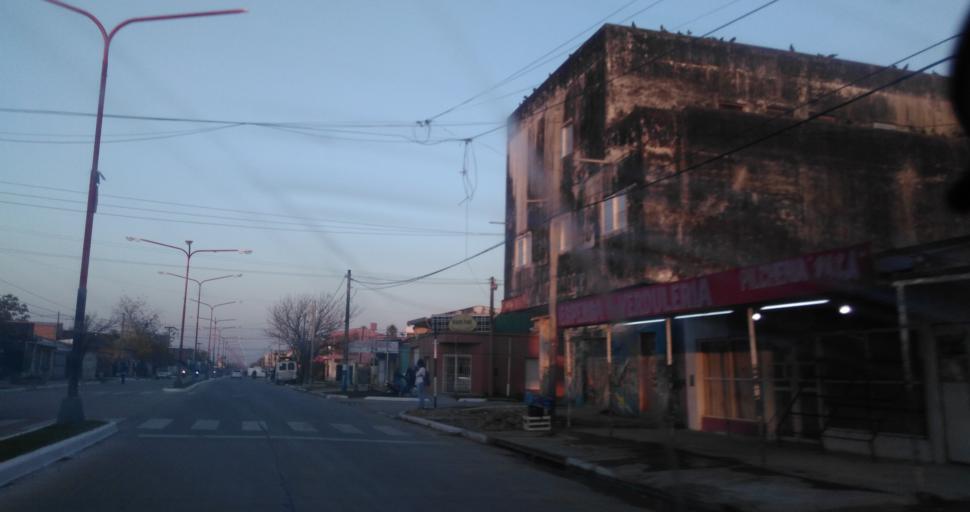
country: AR
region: Chaco
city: Resistencia
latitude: -27.4796
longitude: -58.9755
